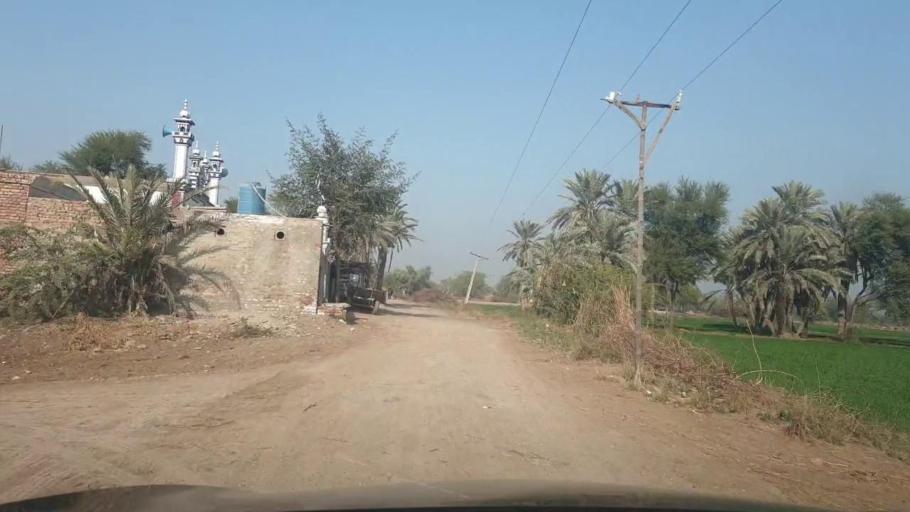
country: PK
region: Sindh
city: Ubauro
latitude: 28.0955
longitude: 69.8411
